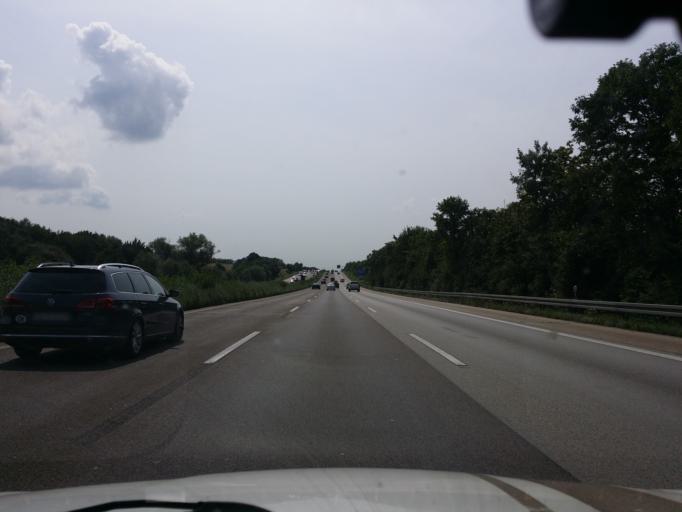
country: DE
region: Hesse
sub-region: Regierungsbezirk Darmstadt
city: Niedernhausen
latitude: 50.1049
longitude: 8.3476
